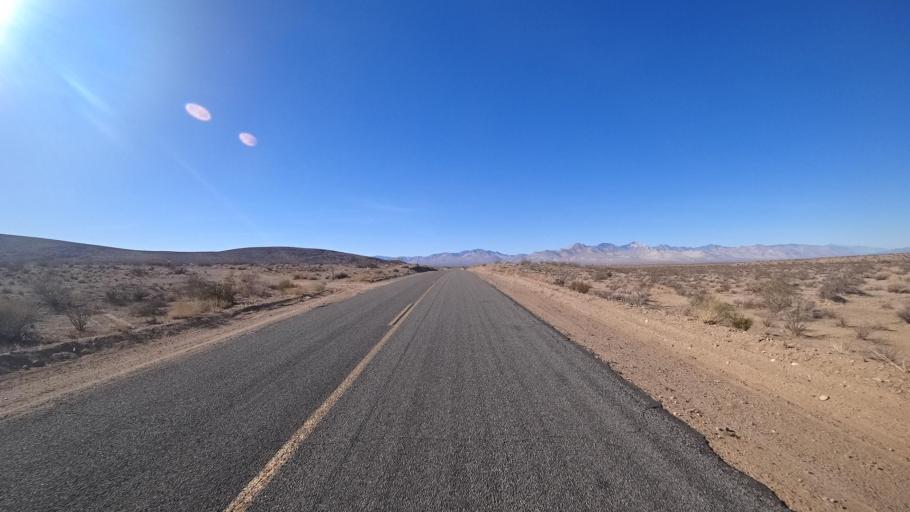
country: US
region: California
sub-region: Kern County
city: China Lake Acres
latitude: 35.5562
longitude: -117.7461
